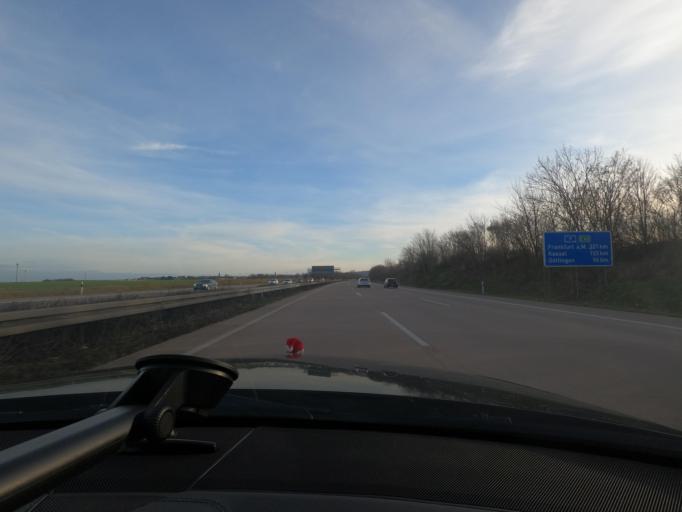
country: DE
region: Lower Saxony
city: Harsum
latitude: 52.1810
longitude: 9.9739
